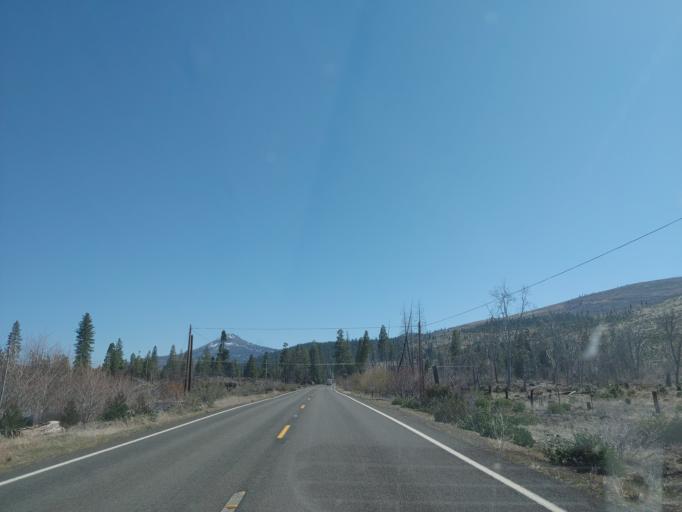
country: US
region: California
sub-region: Shasta County
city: Burney
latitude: 40.7711
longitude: -121.5015
